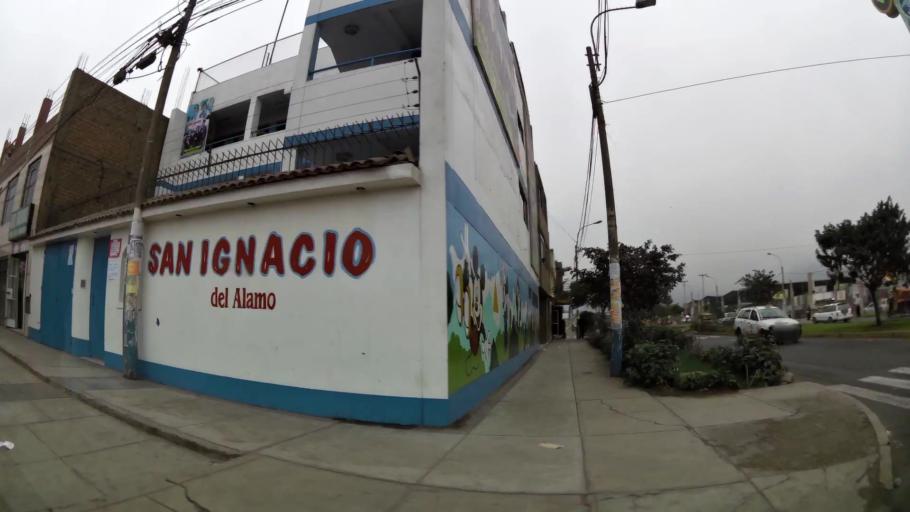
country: PE
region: Lima
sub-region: Lima
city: Independencia
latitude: -11.9378
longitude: -77.0677
